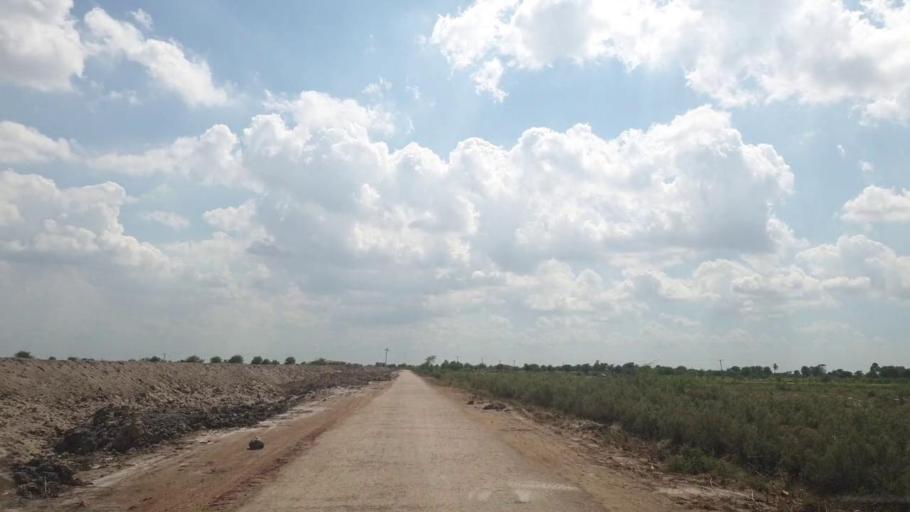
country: PK
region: Sindh
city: Pithoro
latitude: 25.5930
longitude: 69.3998
